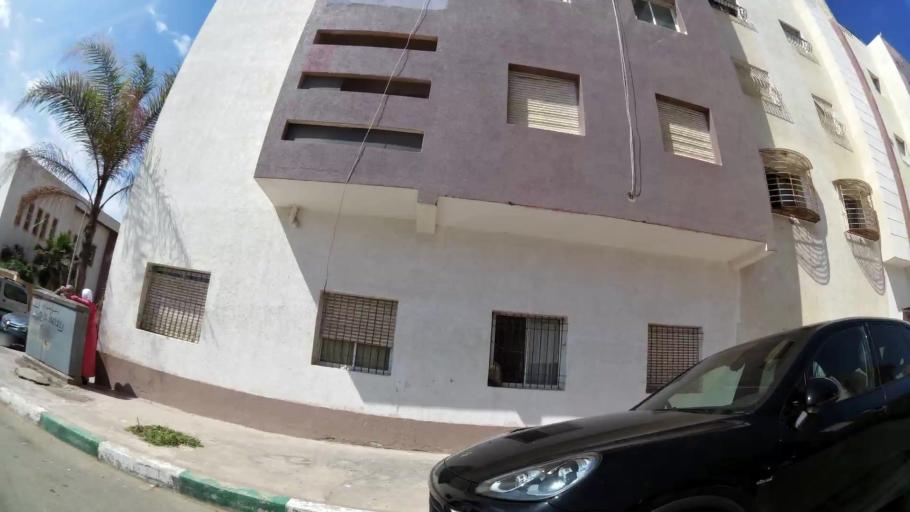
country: MA
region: Rabat-Sale-Zemmour-Zaer
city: Sale
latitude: 34.0817
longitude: -6.7881
